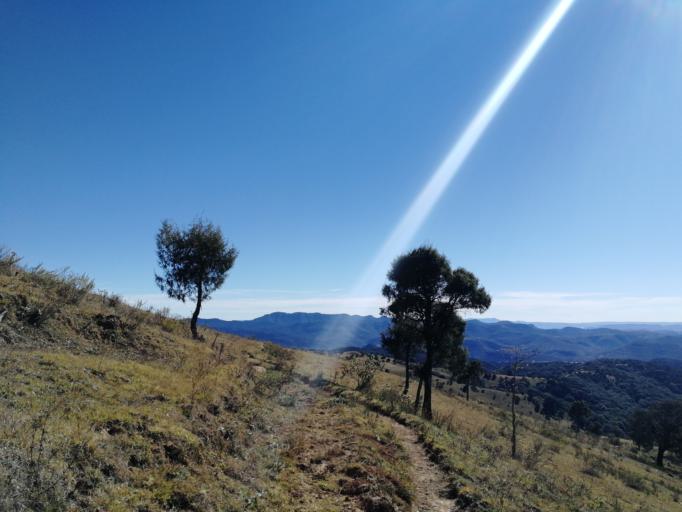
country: MX
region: San Luis Potosi
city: Zaragoza
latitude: 22.0062
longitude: -100.6142
